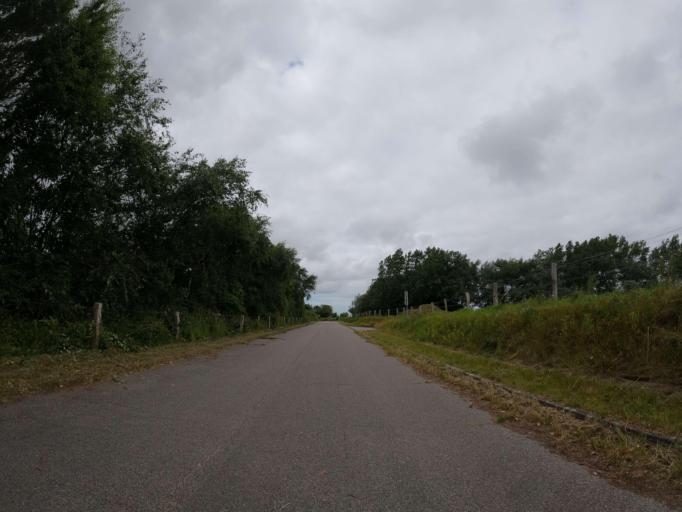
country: DE
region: Schleswig-Holstein
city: Tinnum
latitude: 54.9206
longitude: 8.3461
